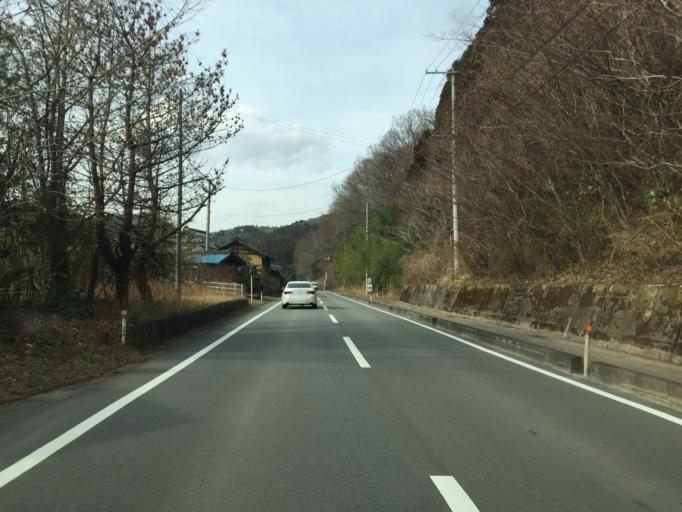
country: JP
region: Fukushima
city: Iwaki
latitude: 36.9995
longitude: 140.7294
